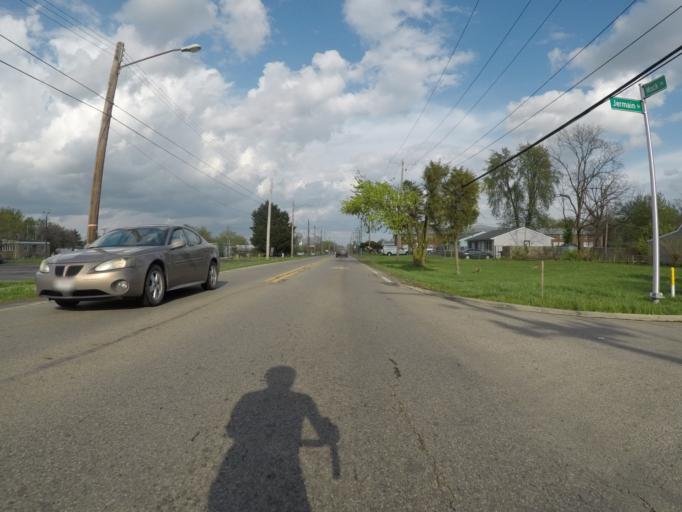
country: US
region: Ohio
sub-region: Franklin County
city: Bexley
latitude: 40.0116
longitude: -82.9521
